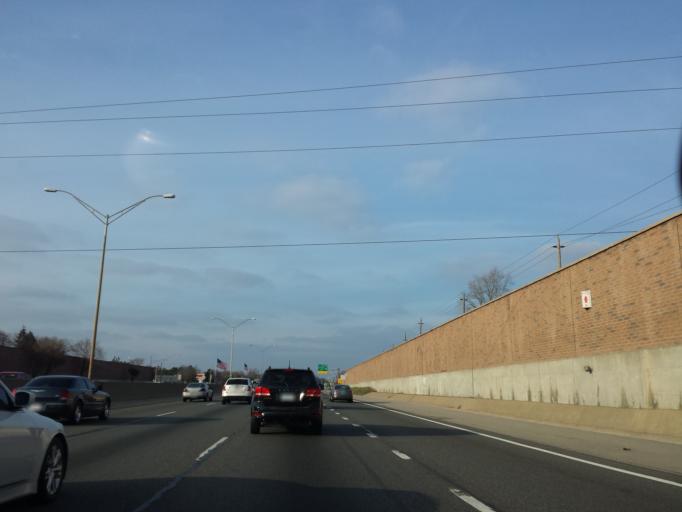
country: US
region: Michigan
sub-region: Oakland County
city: Madison Heights
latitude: 42.4856
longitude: -83.1144
